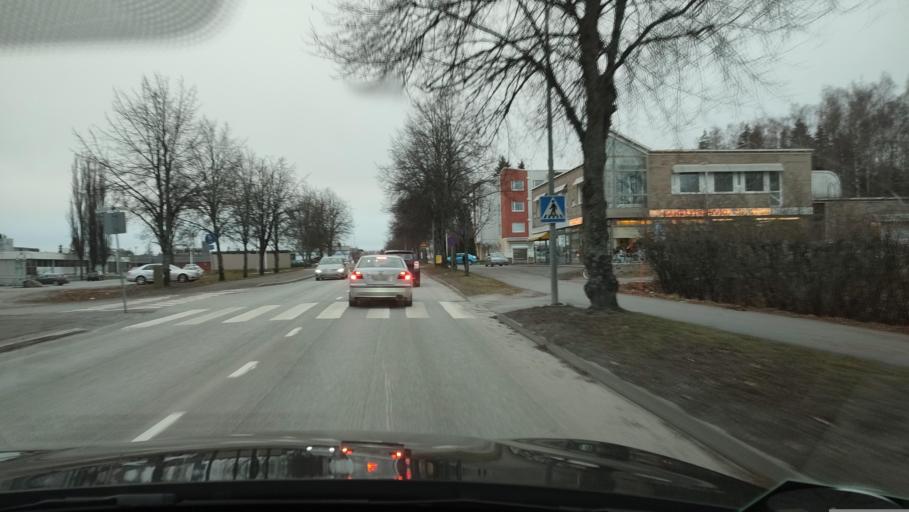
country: FI
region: Southern Ostrobothnia
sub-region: Suupohja
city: Kauhajoki
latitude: 62.4274
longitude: 22.1776
